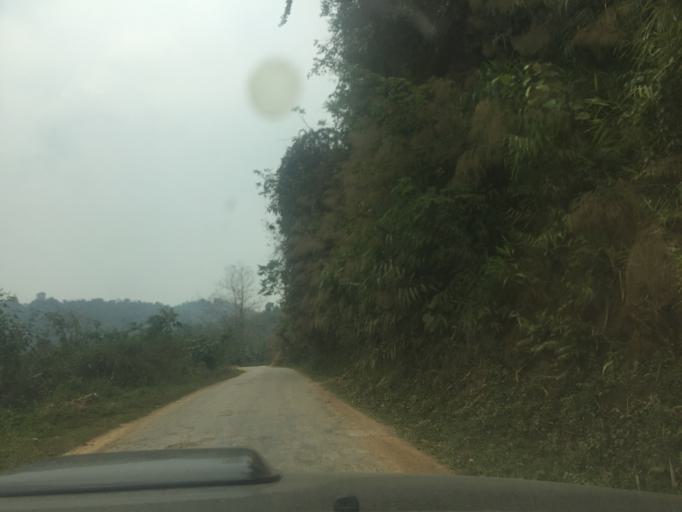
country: LA
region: Vientiane
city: Muang Sanakham
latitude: 18.3937
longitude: 101.5183
